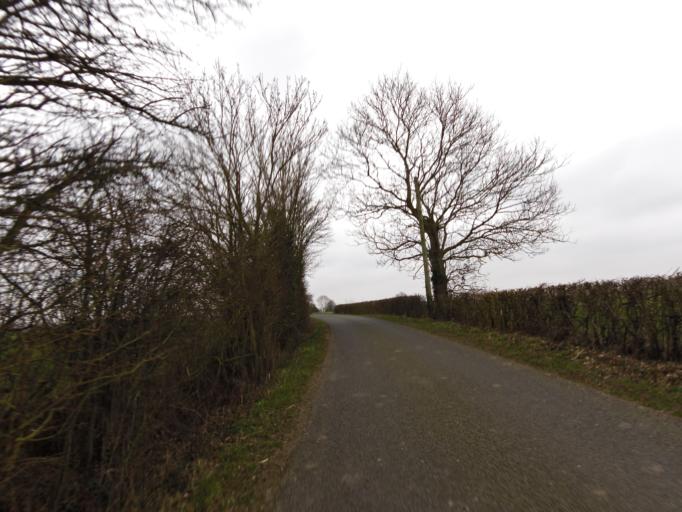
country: GB
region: England
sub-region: Suffolk
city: Framlingham
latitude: 52.2133
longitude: 1.3268
